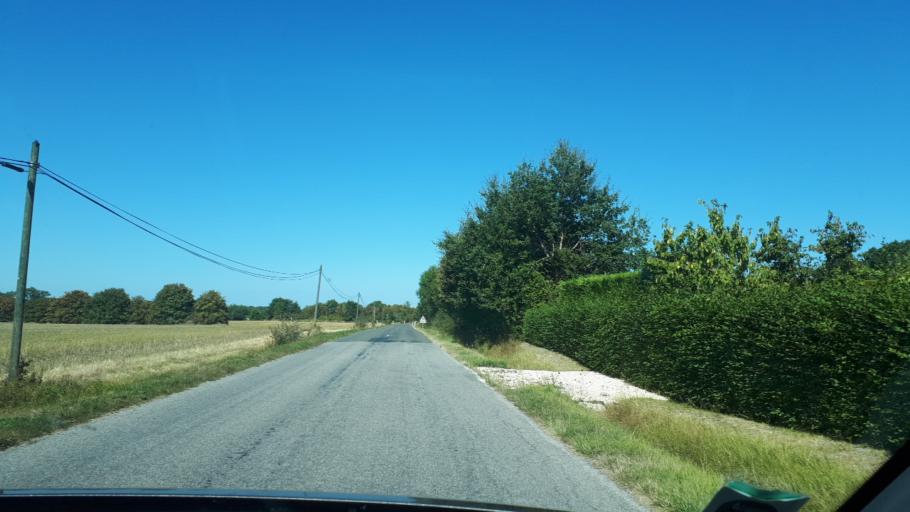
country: FR
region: Centre
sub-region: Departement du Loiret
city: Autry-le-Chatel
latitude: 47.6022
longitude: 2.5983
